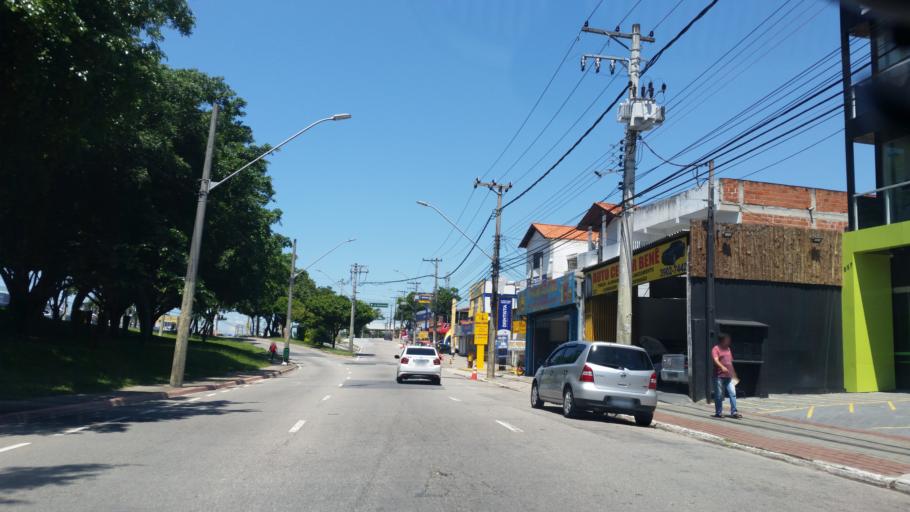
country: BR
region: Sao Paulo
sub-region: Sao Jose Dos Campos
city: Sao Jose dos Campos
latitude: -23.1732
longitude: -45.8152
